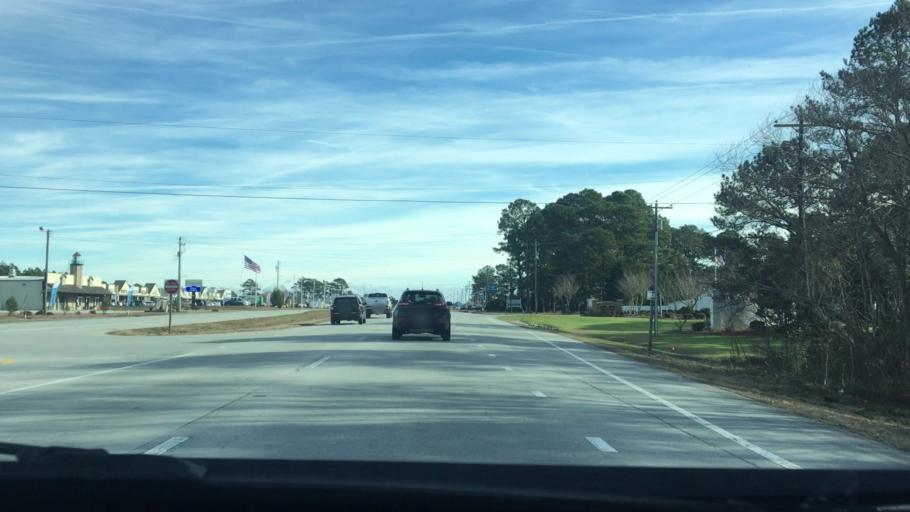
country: US
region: North Carolina
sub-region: Carteret County
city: Pine Knoll Shores
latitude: 34.7436
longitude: -76.8256
